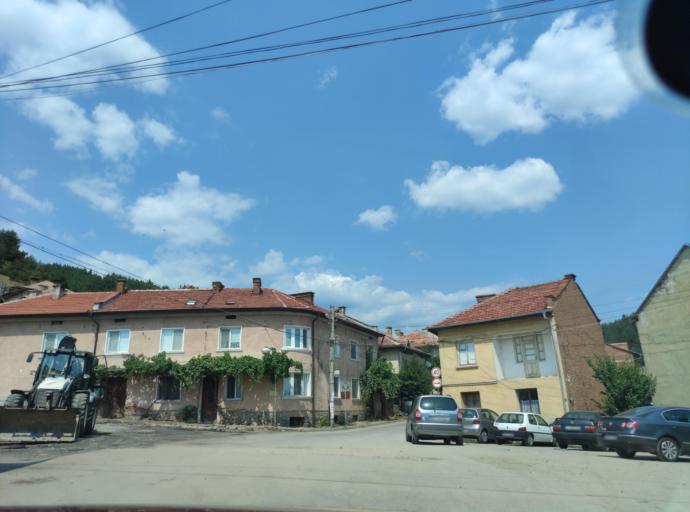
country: BG
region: Blagoevgrad
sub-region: Obshtina Belitsa
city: Belitsa
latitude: 41.9507
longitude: 23.5557
